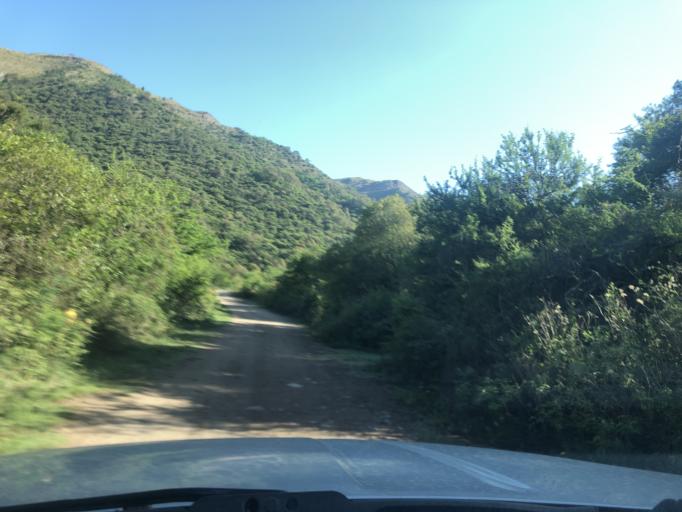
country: AR
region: Cordoba
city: Valle Hermoso
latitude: -31.1157
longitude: -64.4535
